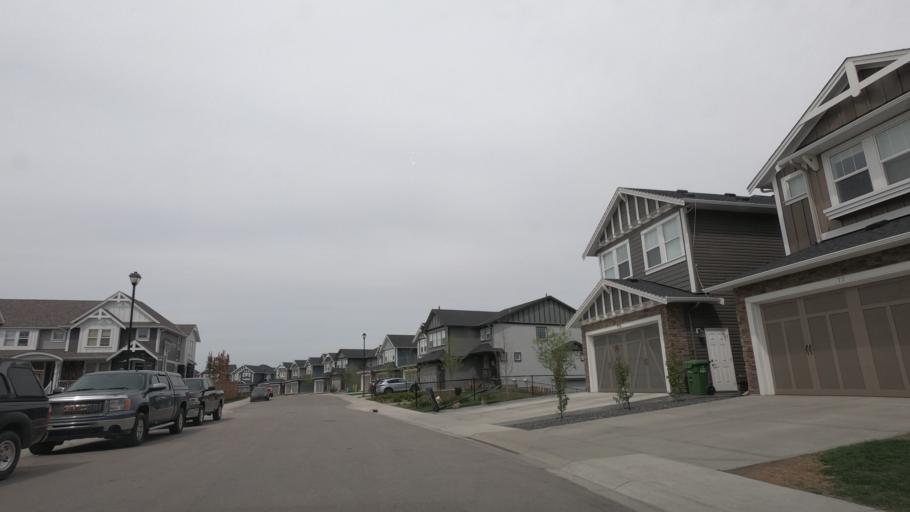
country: CA
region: Alberta
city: Airdrie
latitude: 51.3059
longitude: -114.0315
